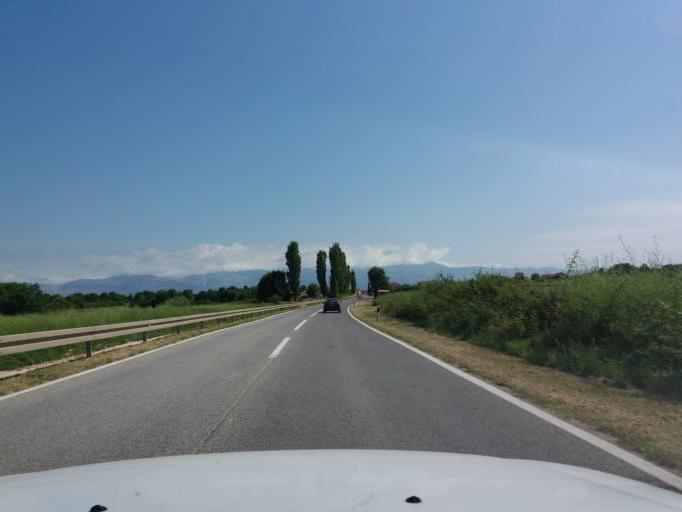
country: HR
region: Zadarska
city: Policnik
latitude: 44.1838
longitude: 15.3940
